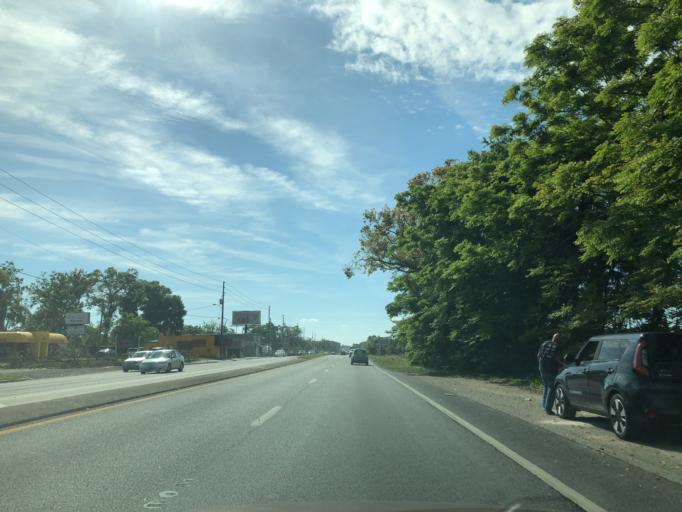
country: US
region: Florida
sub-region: Orange County
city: Zellwood
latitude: 28.7307
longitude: -81.6060
